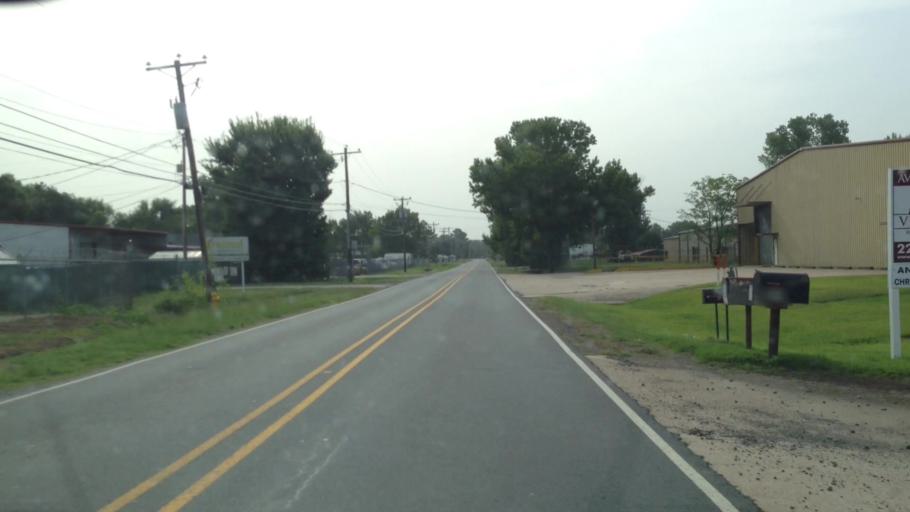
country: US
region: Louisiana
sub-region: De Soto Parish
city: Stonewall
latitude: 32.3663
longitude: -93.8231
